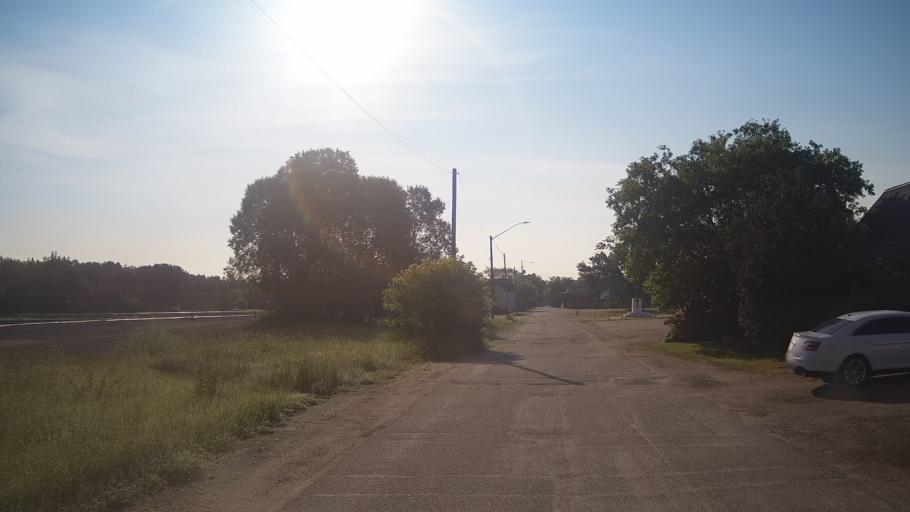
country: CA
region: Ontario
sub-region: Rainy River District
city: Atikokan
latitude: 49.4184
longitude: -91.6642
